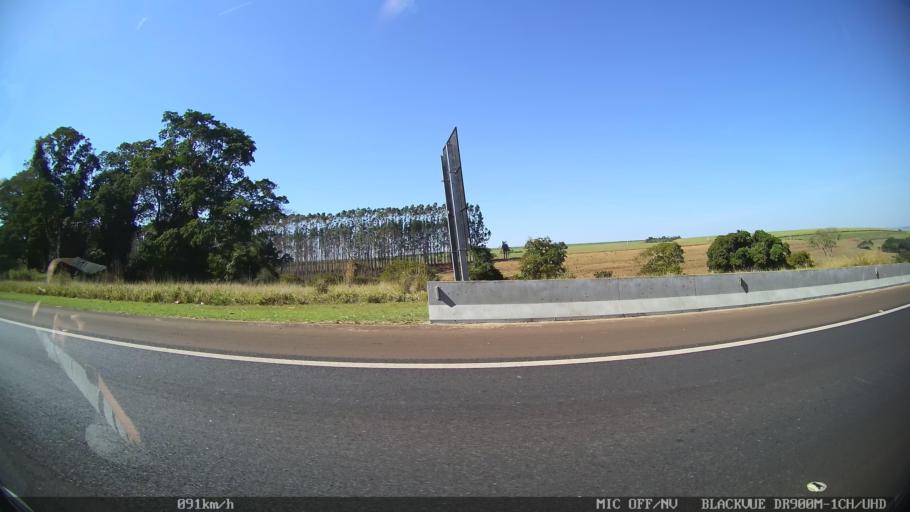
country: BR
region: Sao Paulo
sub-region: Franca
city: Franca
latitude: -20.6942
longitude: -47.4988
